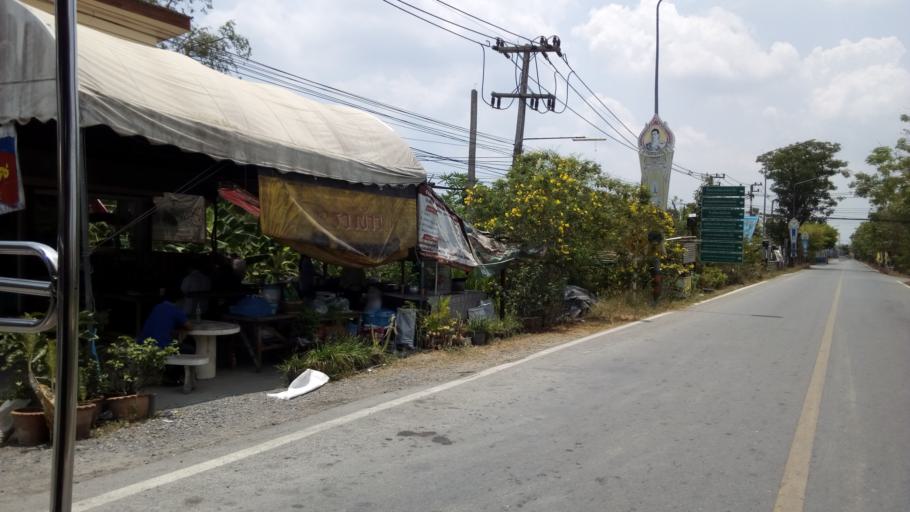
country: TH
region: Pathum Thani
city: Sam Khok
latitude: 14.0981
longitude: 100.5339
